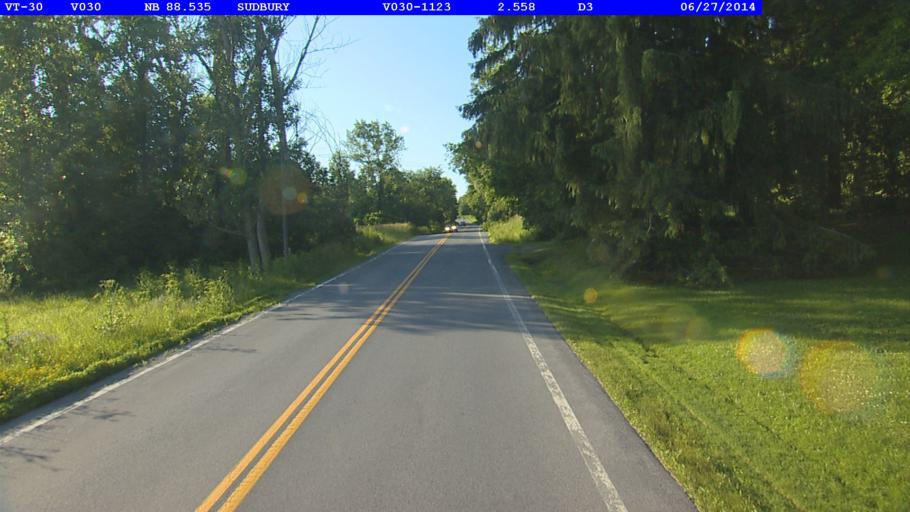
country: US
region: Vermont
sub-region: Rutland County
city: Brandon
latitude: 43.7849
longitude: -73.2031
